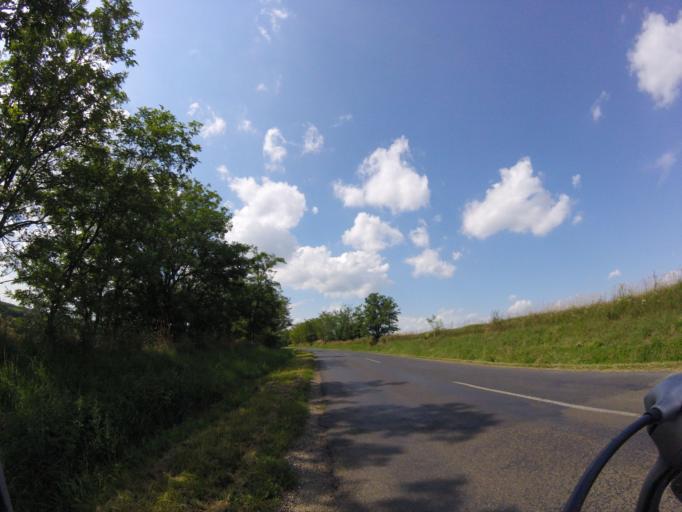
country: HU
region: Somogy
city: Tab
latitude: 46.7125
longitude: 18.0529
